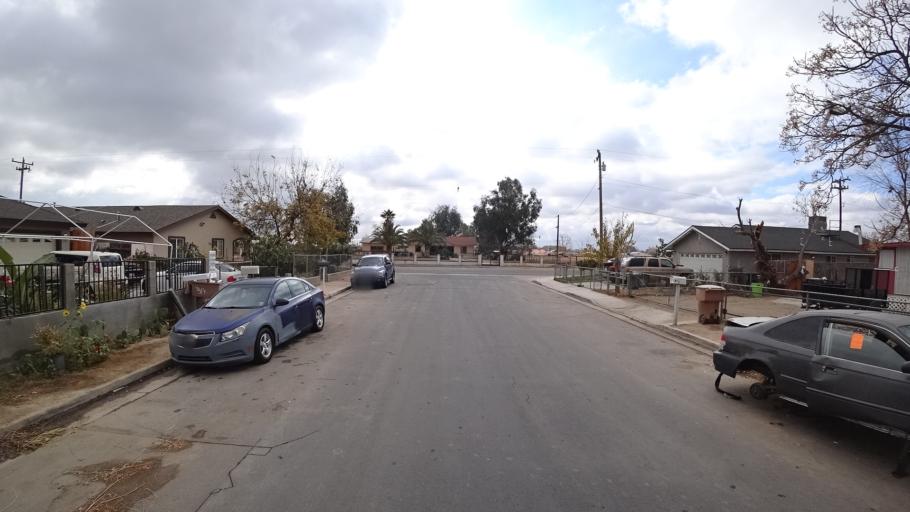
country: US
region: California
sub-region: Kern County
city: Greenfield
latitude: 35.3217
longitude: -118.9909
